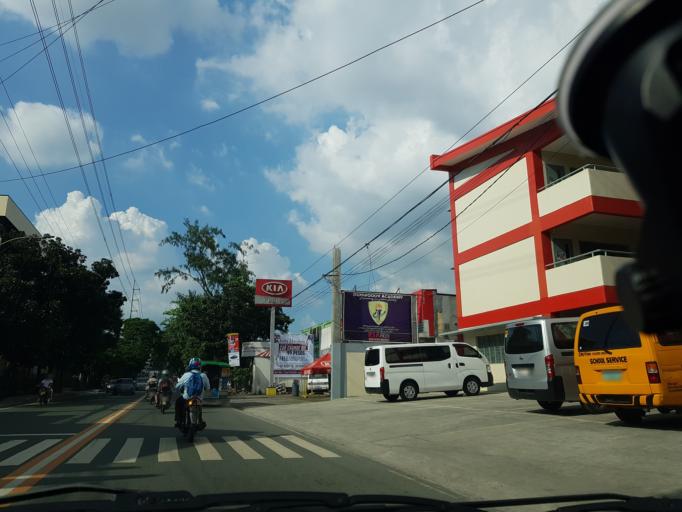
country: PH
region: Metro Manila
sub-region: Marikina
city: Calumpang
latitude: 14.6154
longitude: 121.0924
